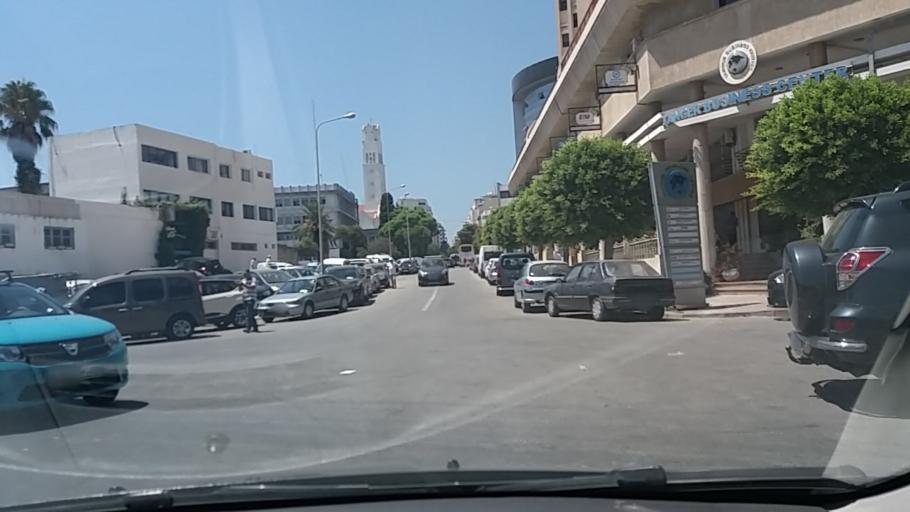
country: MA
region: Tanger-Tetouan
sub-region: Tanger-Assilah
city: Tangier
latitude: 35.7750
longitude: -5.8048
